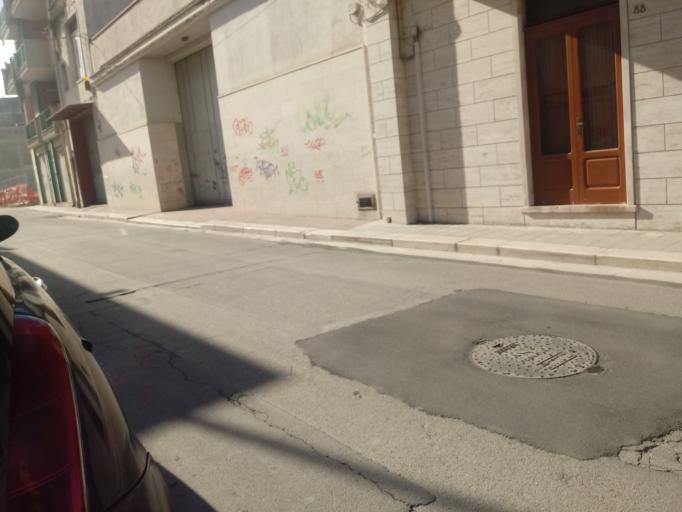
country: IT
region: Apulia
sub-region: Provincia di Barletta - Andria - Trani
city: Andria
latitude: 41.2208
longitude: 16.2955
